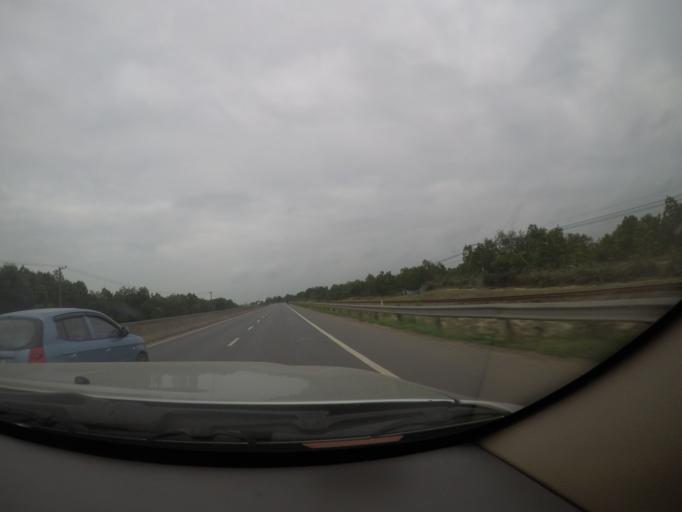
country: VN
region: Quang Tri
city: Hai Lang
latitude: 16.6732
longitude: 107.2625
